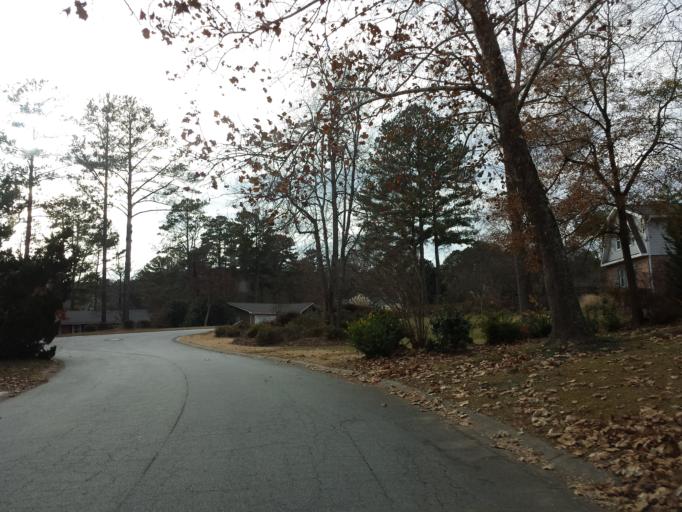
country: US
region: Georgia
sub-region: Fulton County
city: Sandy Springs
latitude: 33.9596
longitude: -84.4262
